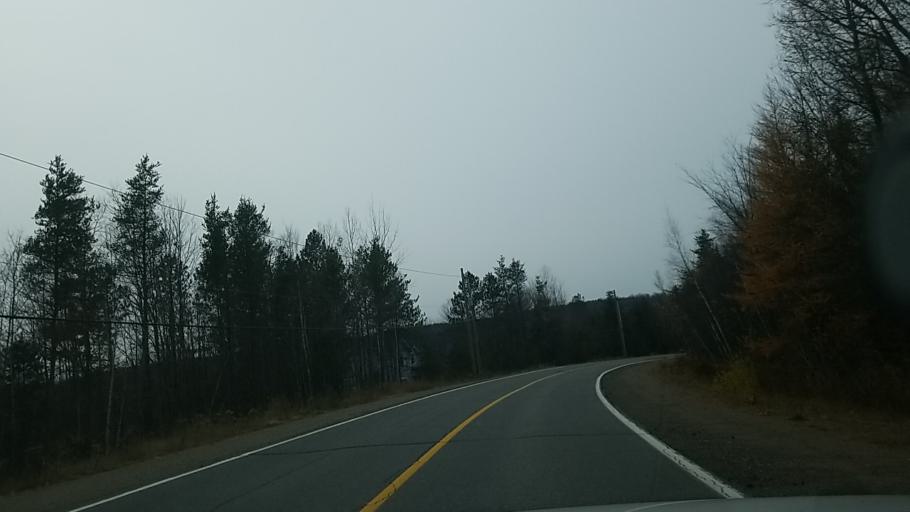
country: CA
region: Quebec
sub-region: Laurentides
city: Saint-Colomban
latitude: 45.7951
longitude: -74.1683
